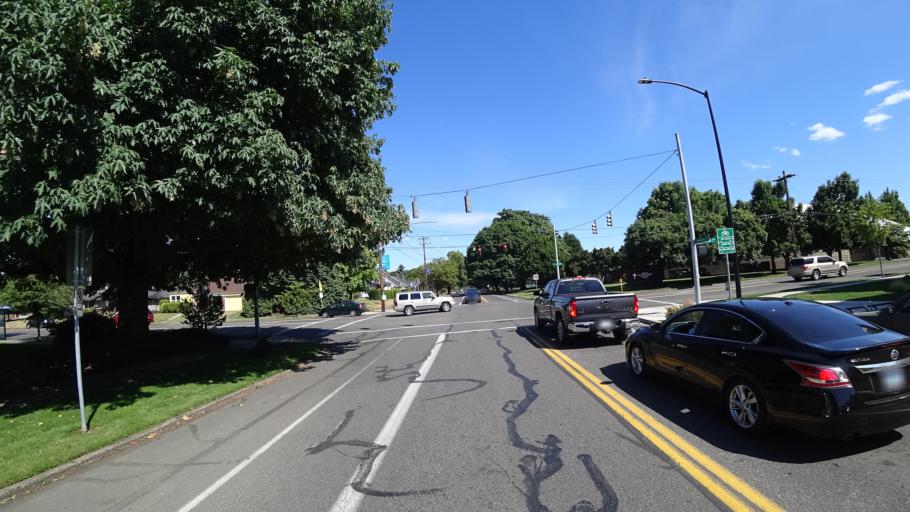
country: US
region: Oregon
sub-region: Washington County
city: West Haven
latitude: 45.5761
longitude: -122.7292
